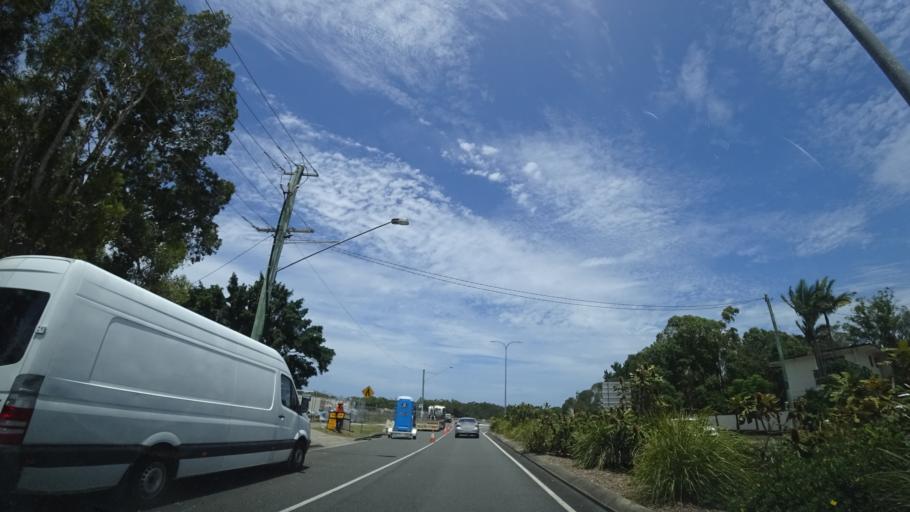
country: AU
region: Queensland
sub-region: Sunshine Coast
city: Mooloolaba
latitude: -26.6109
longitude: 153.0877
